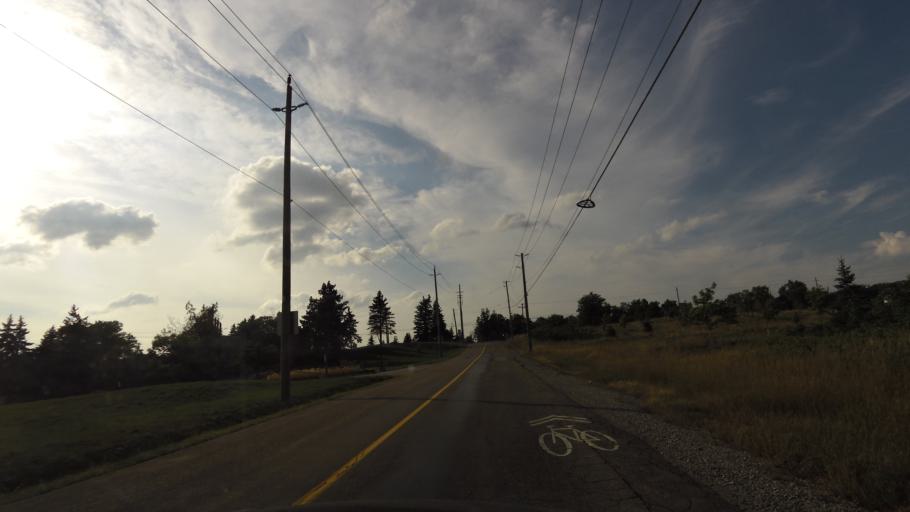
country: CA
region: Ontario
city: Burlington
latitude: 43.3518
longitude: -79.8667
